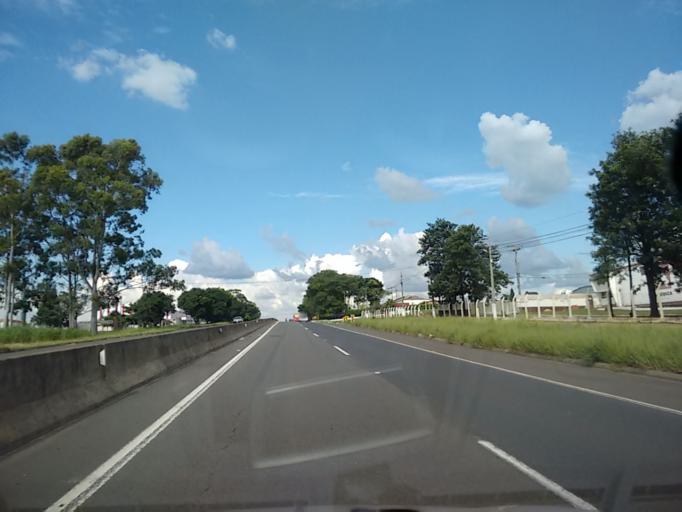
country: BR
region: Sao Paulo
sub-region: Marilia
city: Marilia
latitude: -22.2283
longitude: -49.9060
